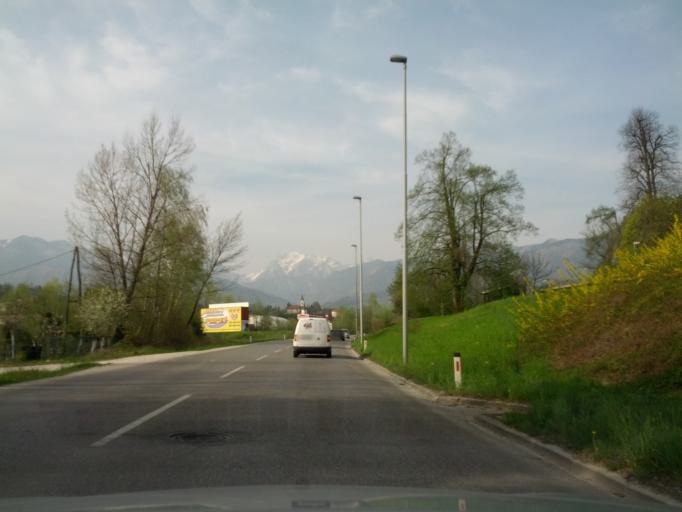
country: SI
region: Kamnik
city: Kamnik
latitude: 46.2149
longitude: 14.6088
